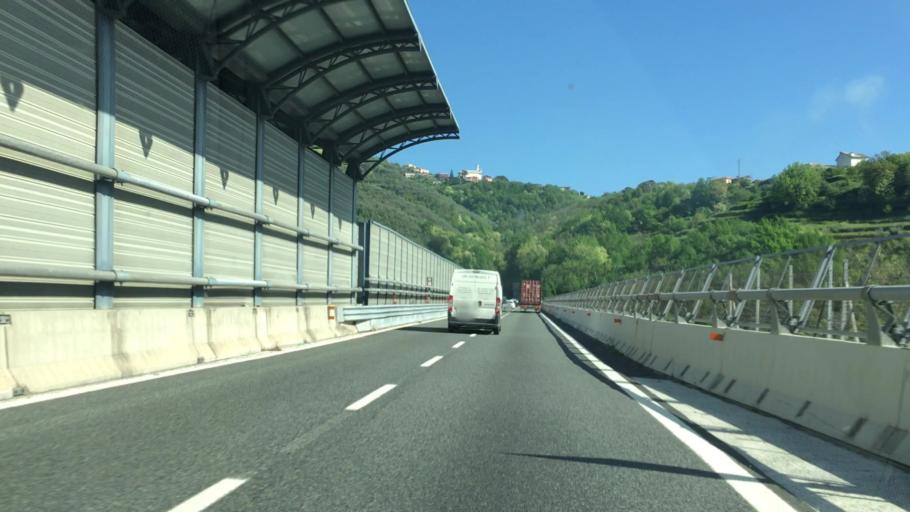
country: IT
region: Liguria
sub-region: Provincia di Genova
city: Lavagna
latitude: 44.3101
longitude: 9.3618
